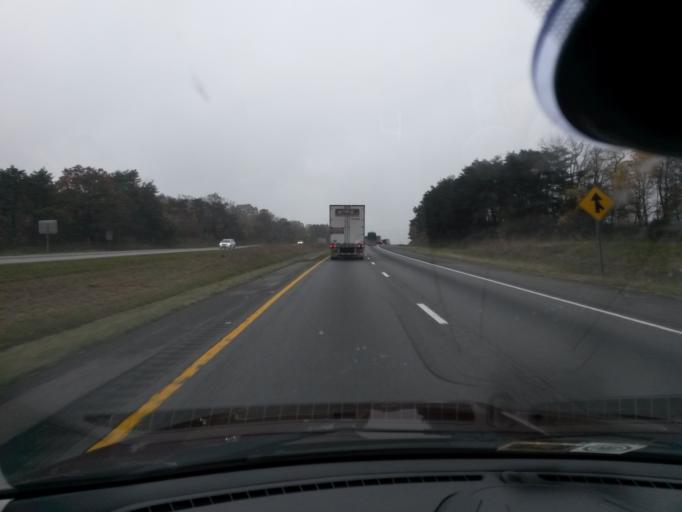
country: US
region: Virginia
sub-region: Montgomery County
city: Shawsville
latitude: 37.2578
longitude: -80.1735
